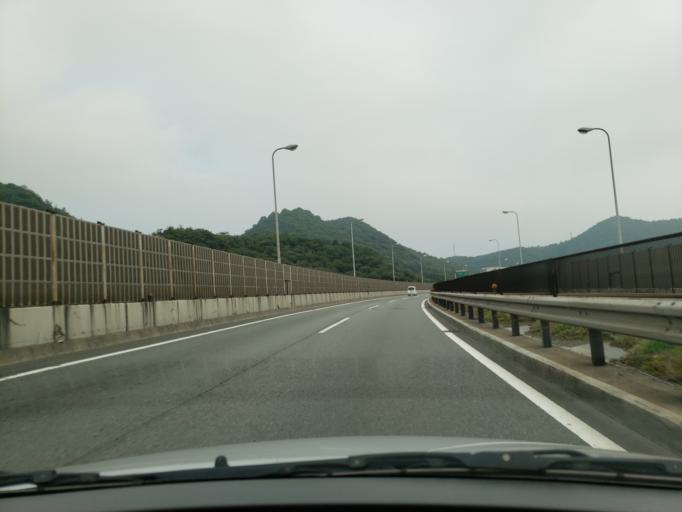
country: JP
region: Hyogo
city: Himeji
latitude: 34.8235
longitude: 134.6365
